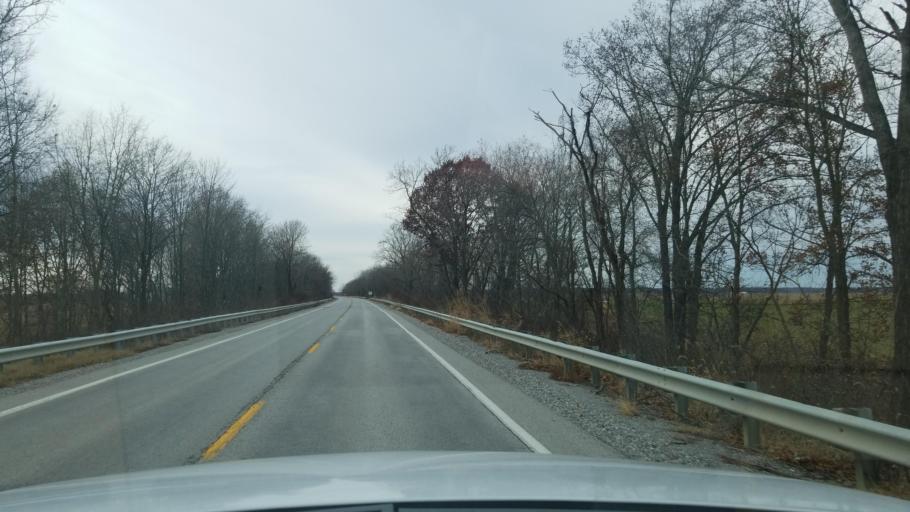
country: US
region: Indiana
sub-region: Posey County
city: Mount Vernon
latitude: 37.9403
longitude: -88.0672
